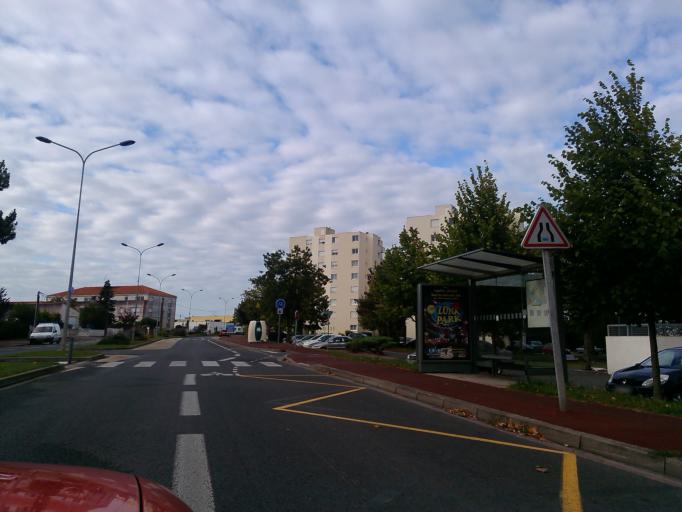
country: FR
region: Poitou-Charentes
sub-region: Departement de la Charente-Maritime
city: Royan
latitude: 45.6350
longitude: -1.0291
